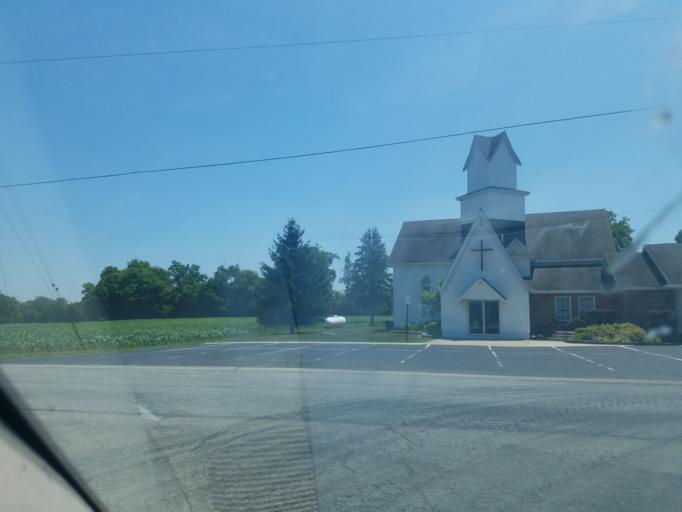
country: US
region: Ohio
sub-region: Allen County
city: Delphos
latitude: 40.7794
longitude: -84.3079
